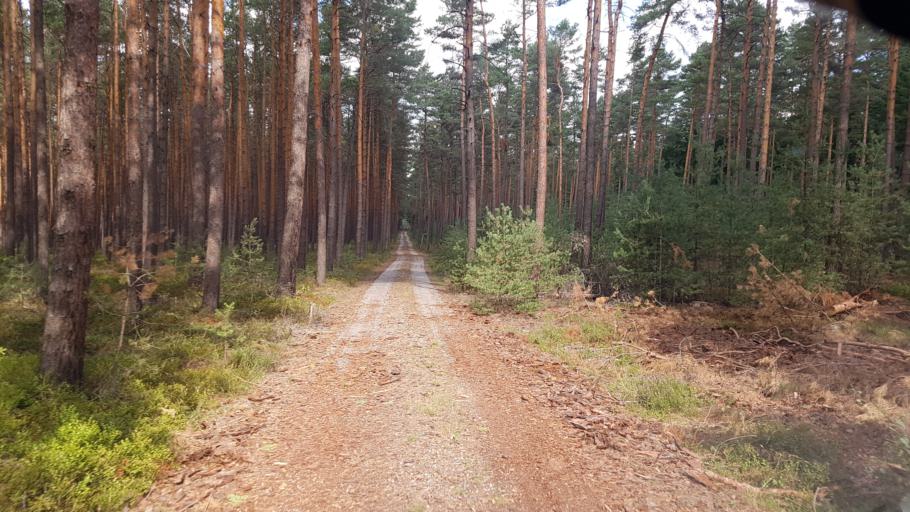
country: DE
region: Brandenburg
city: Crinitz
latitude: 51.7053
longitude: 13.7681
